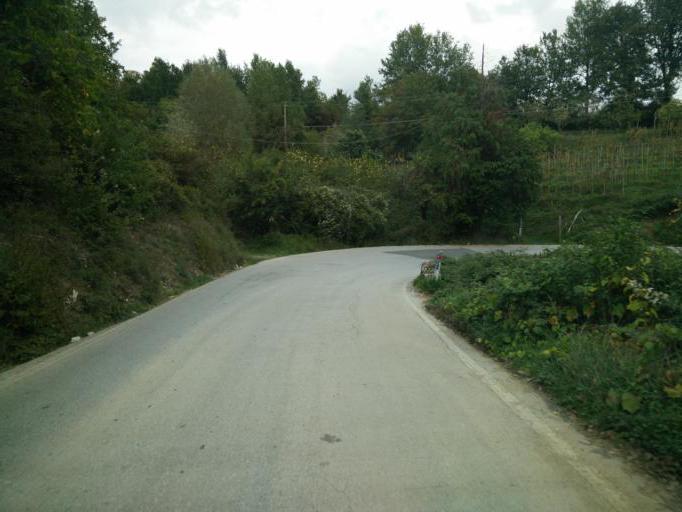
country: IT
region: Tuscany
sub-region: Provincia di Massa-Carrara
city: Fivizzano
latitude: 44.2071
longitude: 10.0911
